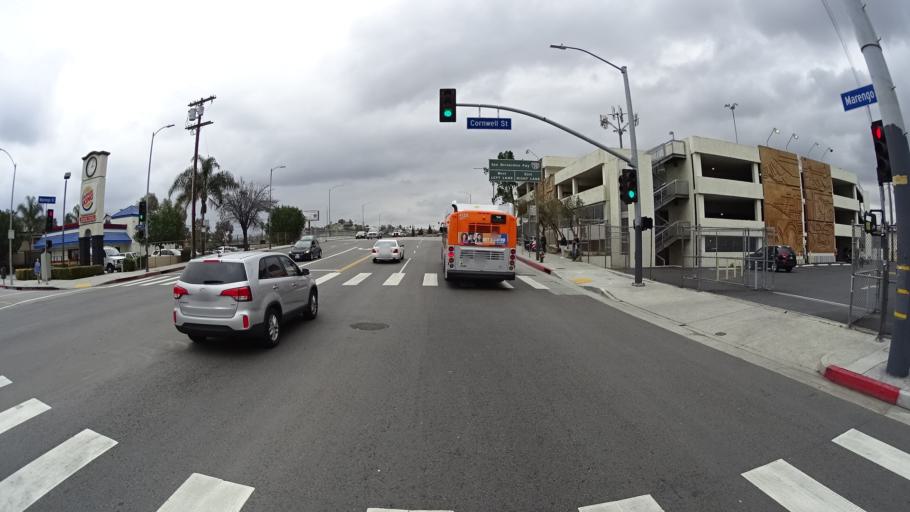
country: US
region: California
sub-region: Los Angeles County
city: Boyle Heights
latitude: 34.0557
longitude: -118.2051
